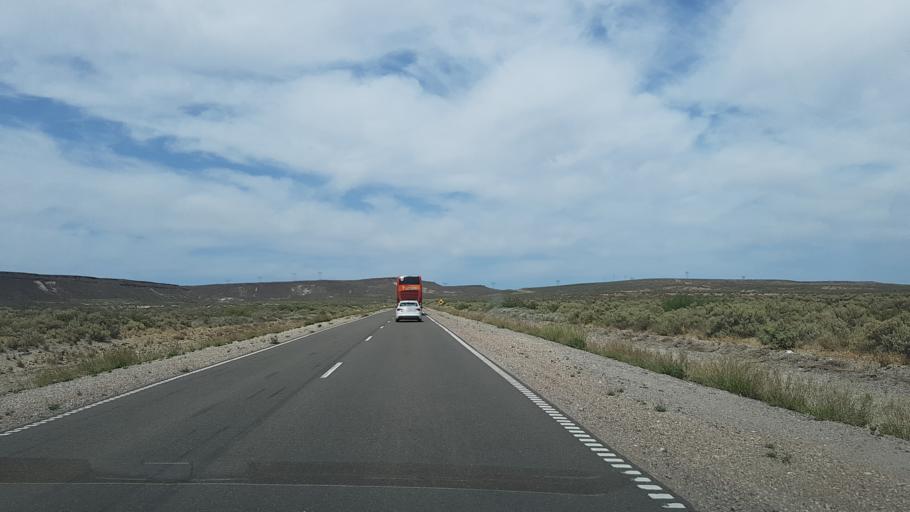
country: AR
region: Neuquen
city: Piedra del Aguila
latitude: -39.9650
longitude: -70.0094
